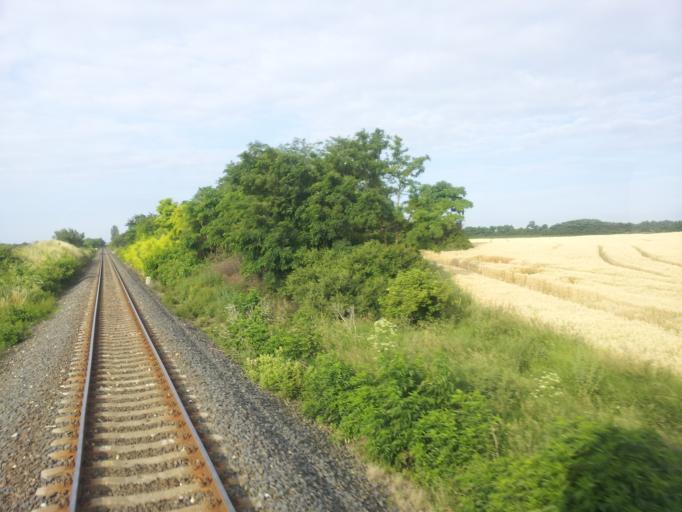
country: HU
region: Fejer
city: Polgardi
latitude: 47.0604
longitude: 18.2729
